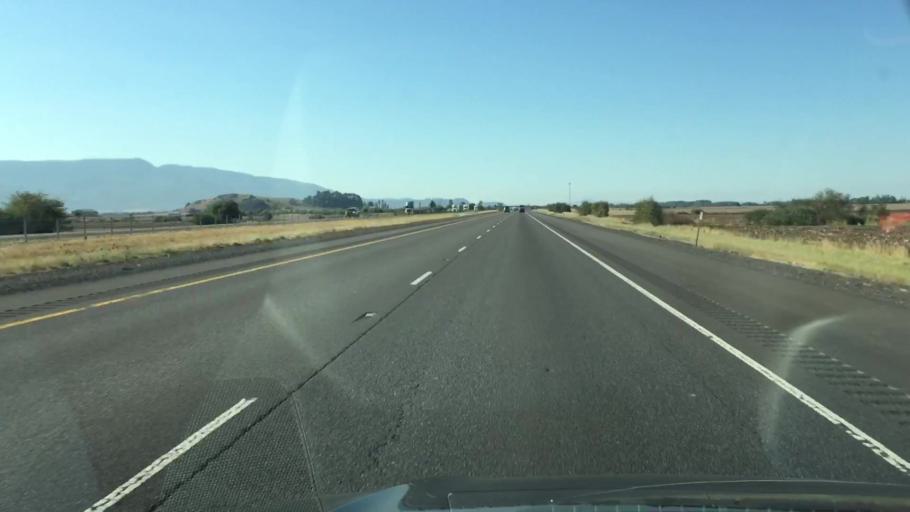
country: US
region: Oregon
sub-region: Linn County
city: Brownsville
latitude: 44.3420
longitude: -123.0614
